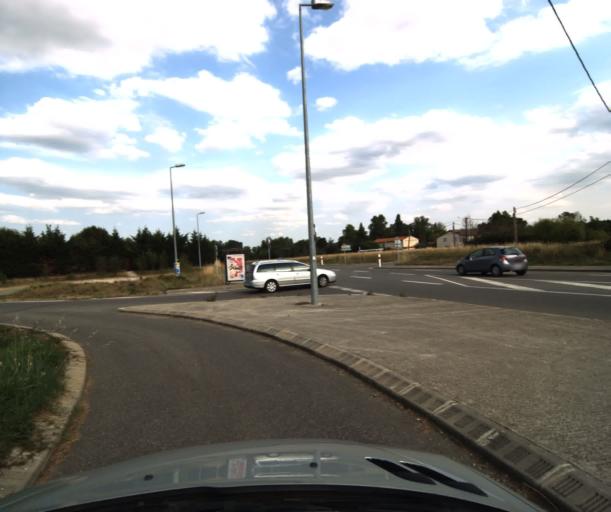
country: FR
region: Midi-Pyrenees
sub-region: Departement de la Haute-Garonne
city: Fonsorbes
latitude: 43.5132
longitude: 1.2126
